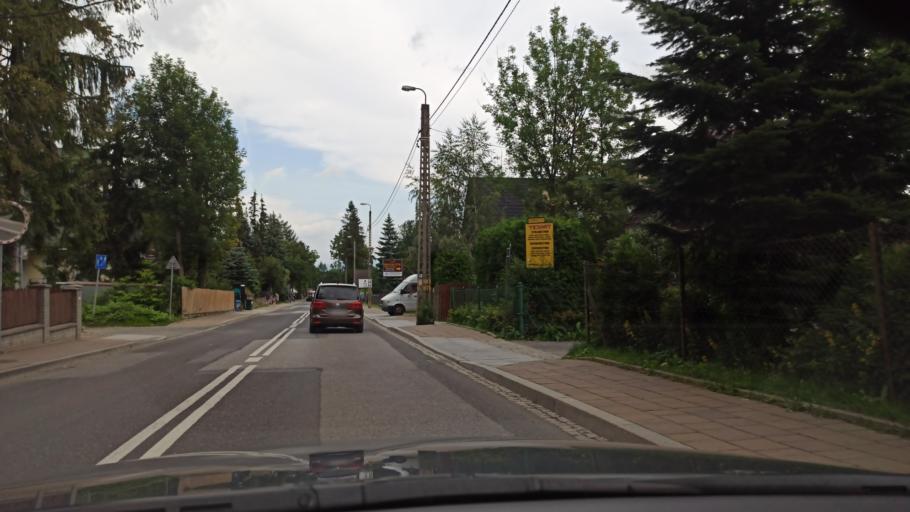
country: PL
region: Lesser Poland Voivodeship
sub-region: Powiat tatrzanski
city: Zakopane
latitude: 49.2890
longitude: 19.9806
